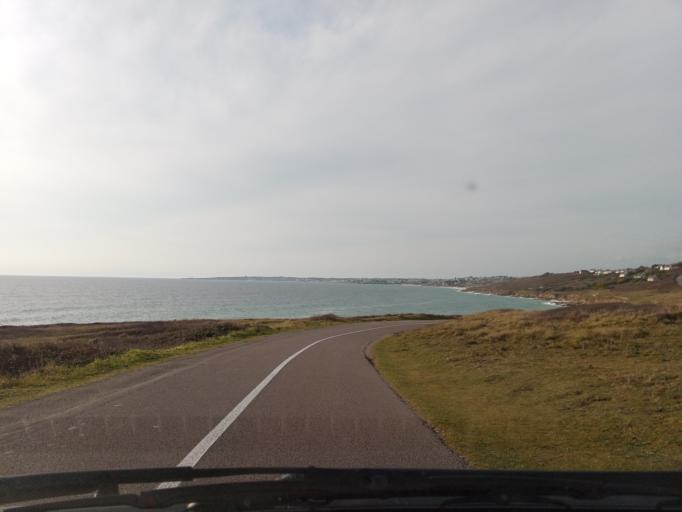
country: FR
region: Brittany
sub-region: Departement du Finistere
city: Plouhinec
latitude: 47.9889
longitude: -4.4769
